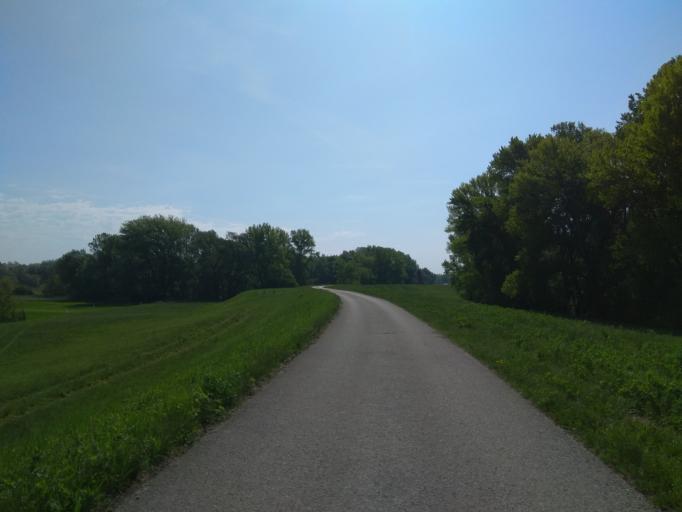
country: SK
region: Trnavsky
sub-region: Okres Dunajska Streda
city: Velky Meder
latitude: 47.7945
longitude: 17.6828
